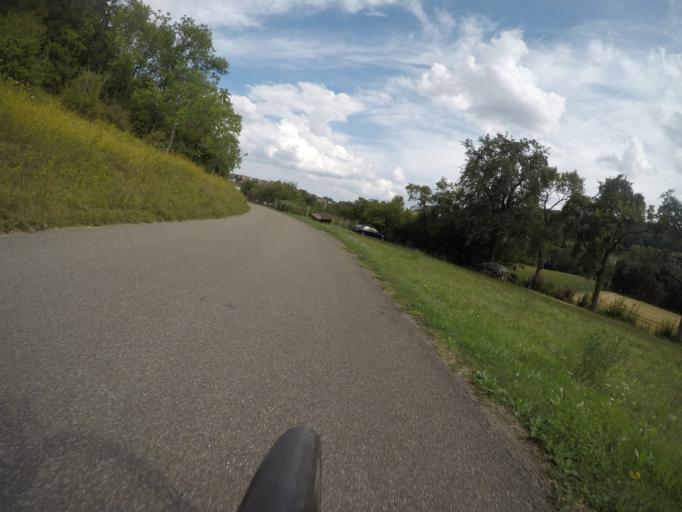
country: DE
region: Baden-Wuerttemberg
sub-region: Regierungsbezirk Stuttgart
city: Weil der Stadt
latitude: 48.7288
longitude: 8.8848
